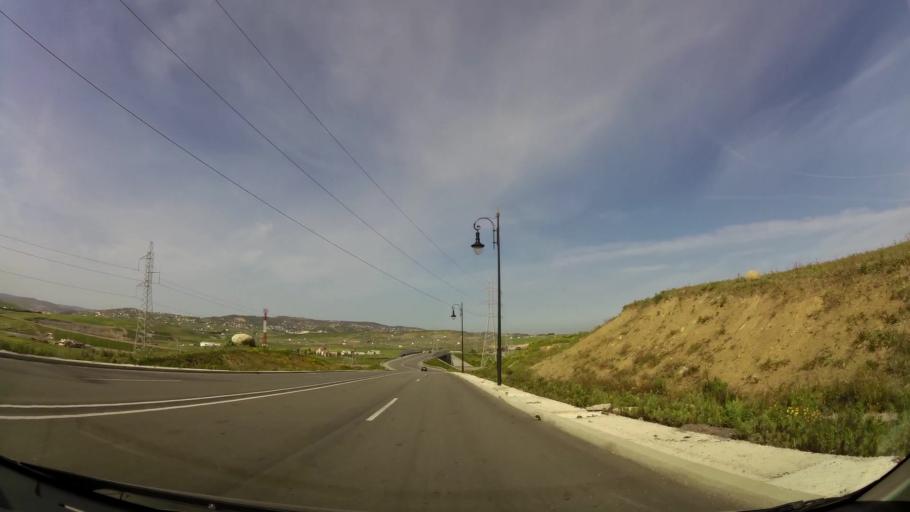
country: MA
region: Tanger-Tetouan
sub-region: Tanger-Assilah
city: Tangier
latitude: 35.7017
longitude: -5.7971
